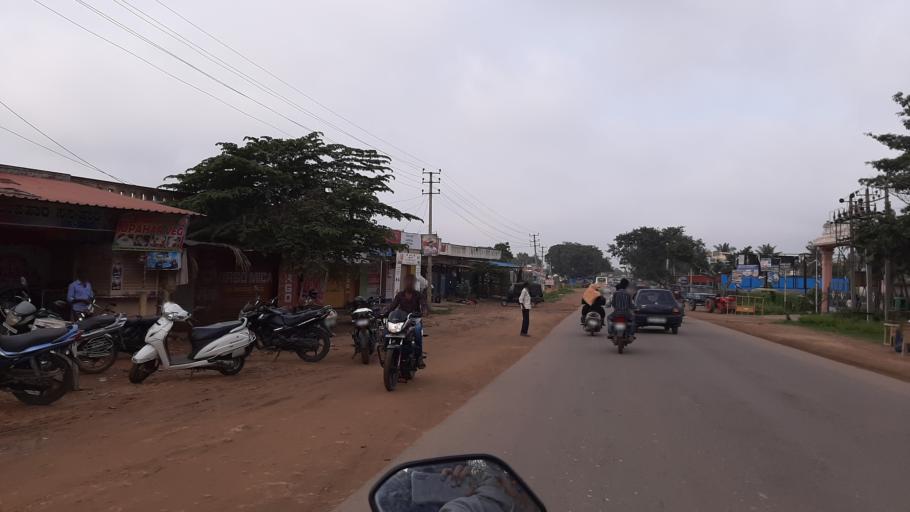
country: IN
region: Karnataka
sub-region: Bangalore Rural
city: Nelamangala
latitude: 12.9852
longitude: 77.4457
